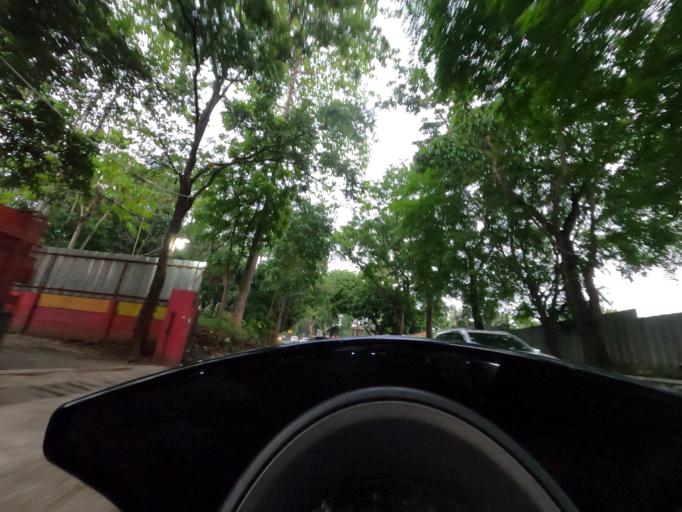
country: ID
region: West Java
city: Lembang
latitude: -6.5833
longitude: 107.7438
